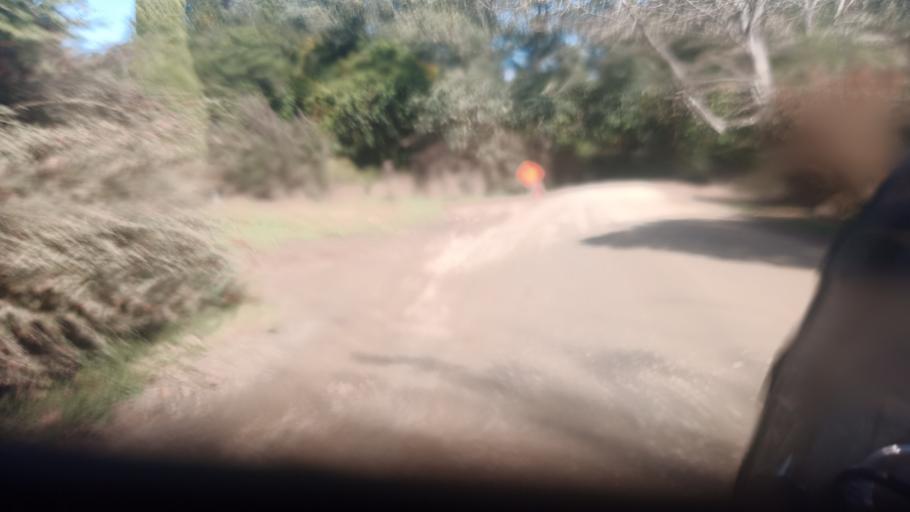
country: NZ
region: Bay of Plenty
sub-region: Opotiki District
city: Opotiki
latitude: -38.4169
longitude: 177.5602
